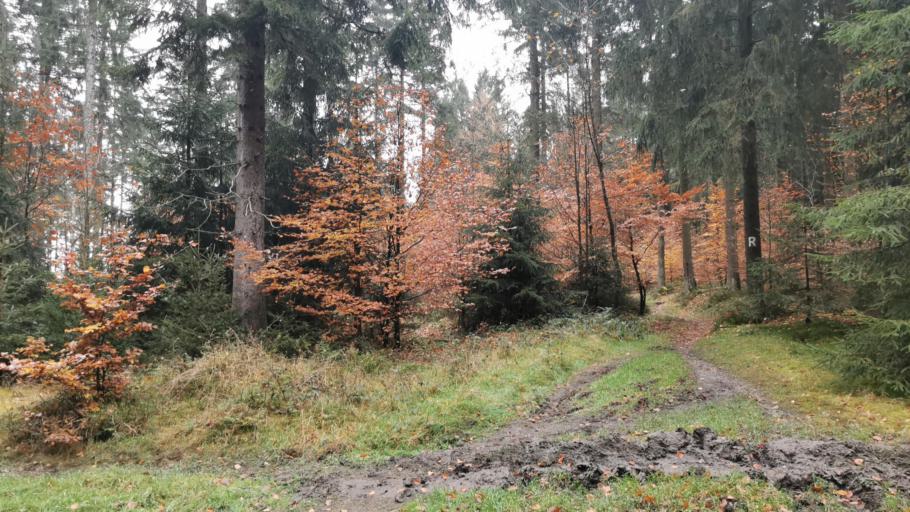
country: DE
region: Thuringia
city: Wurzbach
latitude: 50.4278
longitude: 11.5104
